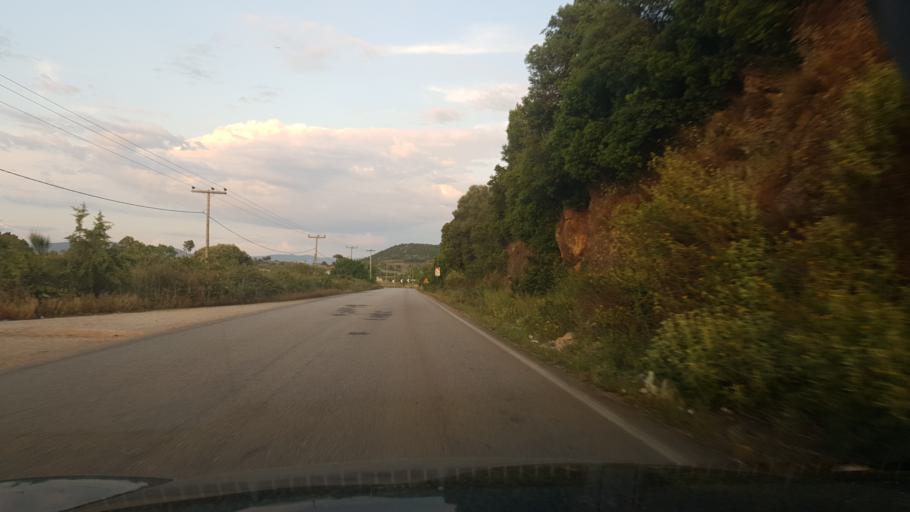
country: GR
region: Ionian Islands
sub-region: Lefkada
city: Lefkada
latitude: 38.8634
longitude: 20.7854
